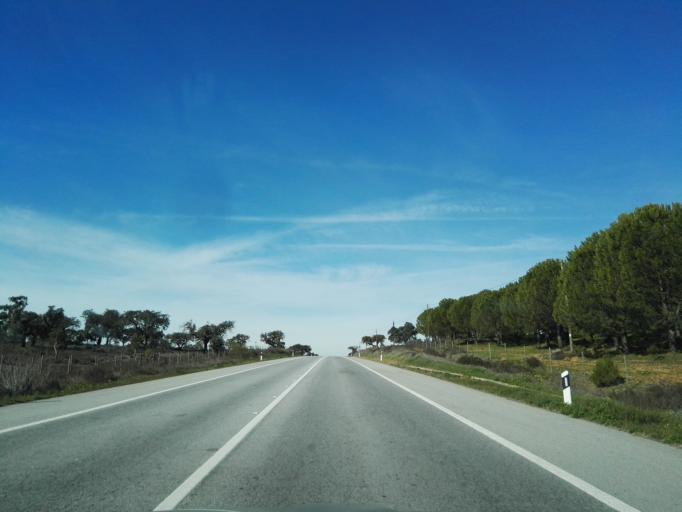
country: PT
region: Portalegre
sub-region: Arronches
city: Arronches
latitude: 39.1482
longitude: -7.3075
